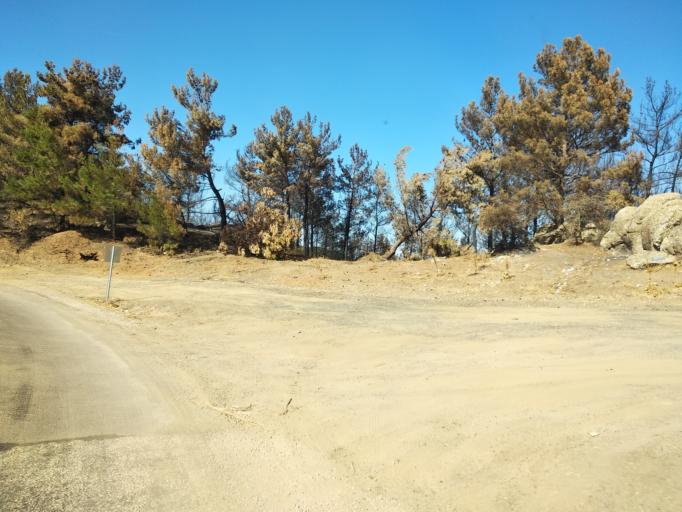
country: TR
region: Izmir
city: Gaziemir
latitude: 38.3057
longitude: 26.9993
